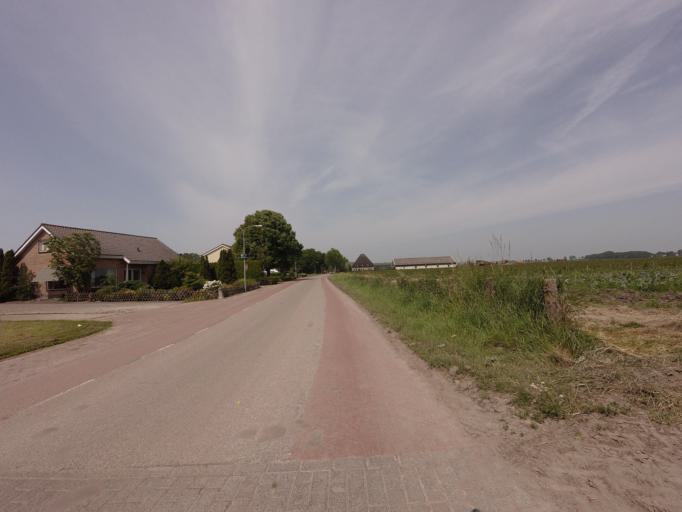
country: NL
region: North Holland
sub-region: Gemeente Hoorn
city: Hoorn
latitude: 52.6893
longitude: 5.0157
